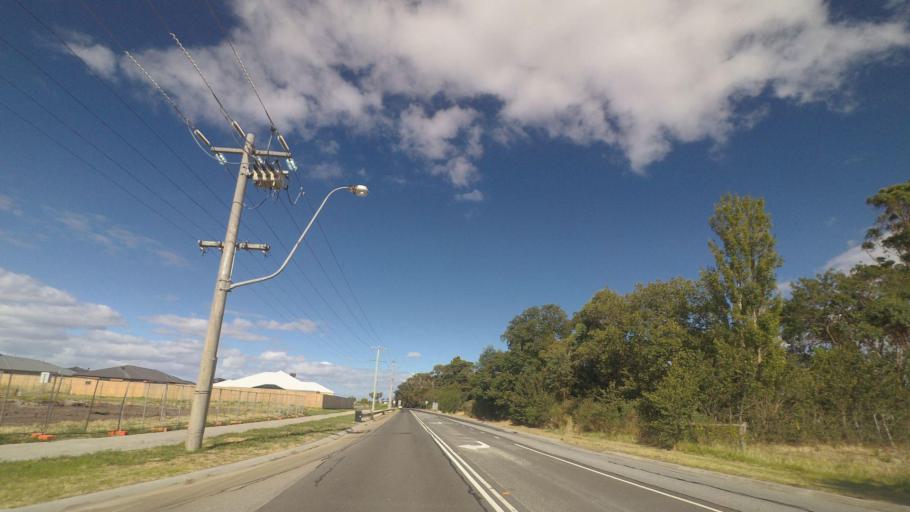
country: AU
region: Victoria
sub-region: Cardinia
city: Koo-Wee-Rup
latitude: -38.2028
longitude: 145.4824
